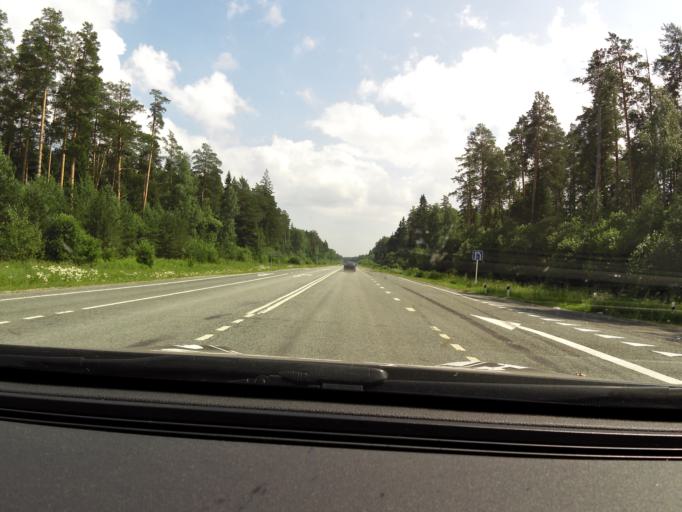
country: RU
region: Sverdlovsk
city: Achit
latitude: 56.8113
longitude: 57.8269
